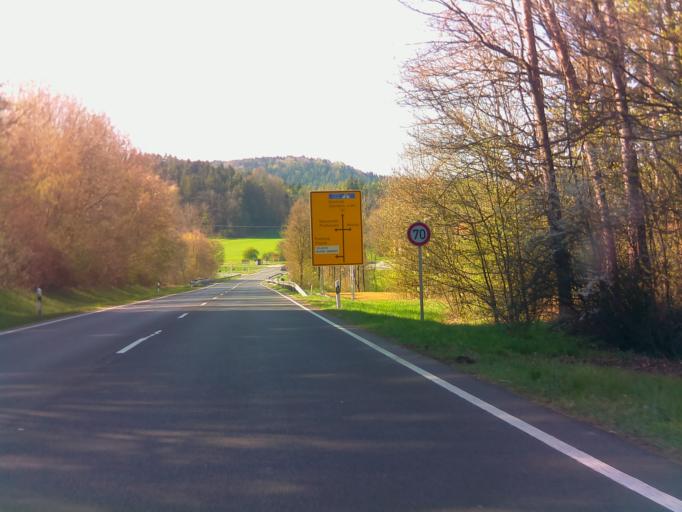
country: DE
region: Bavaria
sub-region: Upper Palatinate
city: Edelsfeld
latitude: 49.5998
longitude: 11.6835
